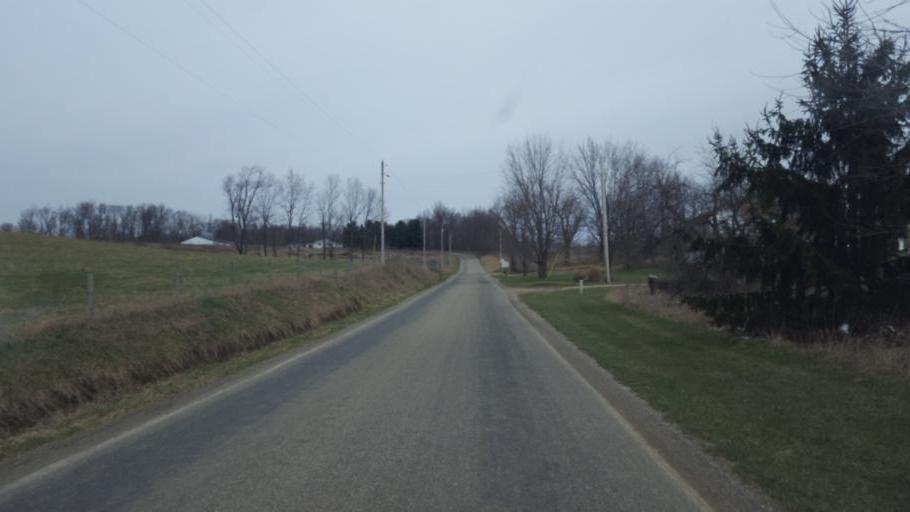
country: US
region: Ohio
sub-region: Knox County
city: Danville
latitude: 40.5136
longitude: -82.3813
